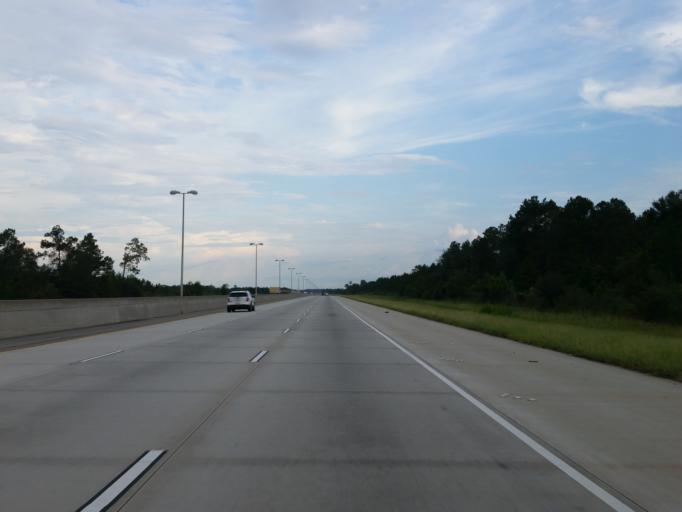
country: US
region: Georgia
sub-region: Cook County
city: Adel
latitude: 31.0859
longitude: -83.4139
